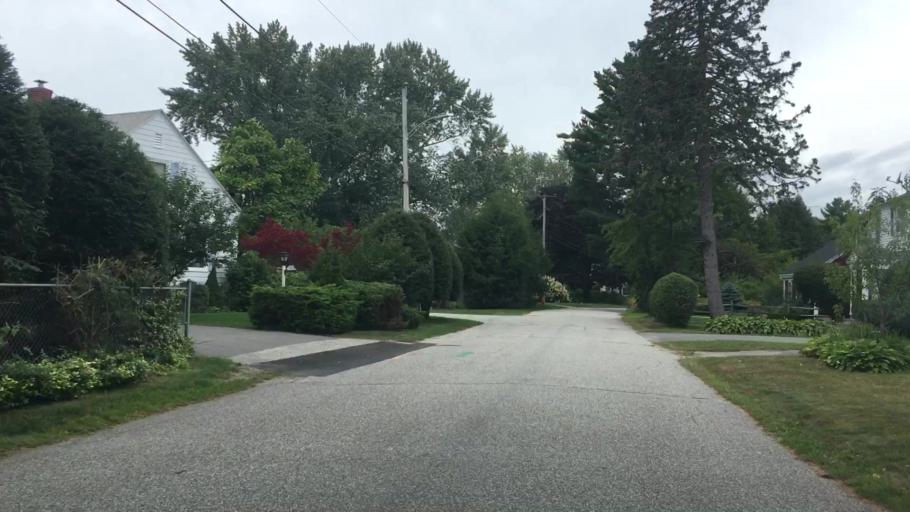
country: US
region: Maine
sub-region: Cumberland County
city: Falmouth
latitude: 43.6983
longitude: -70.2419
